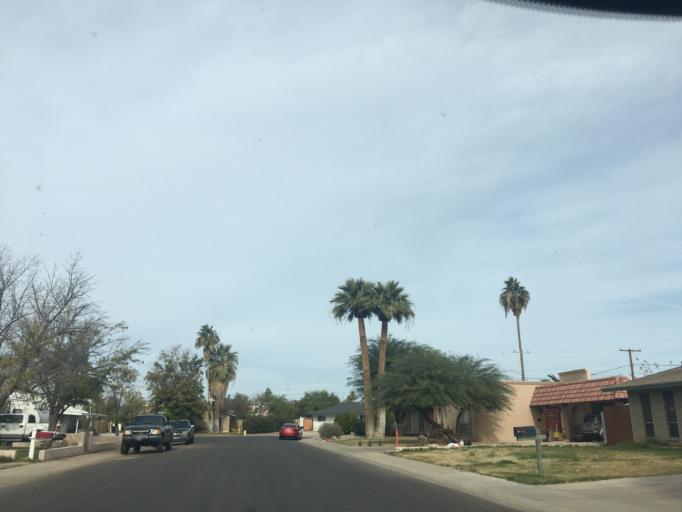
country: US
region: Arizona
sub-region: Maricopa County
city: Gilbert
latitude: 33.3488
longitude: -111.7961
